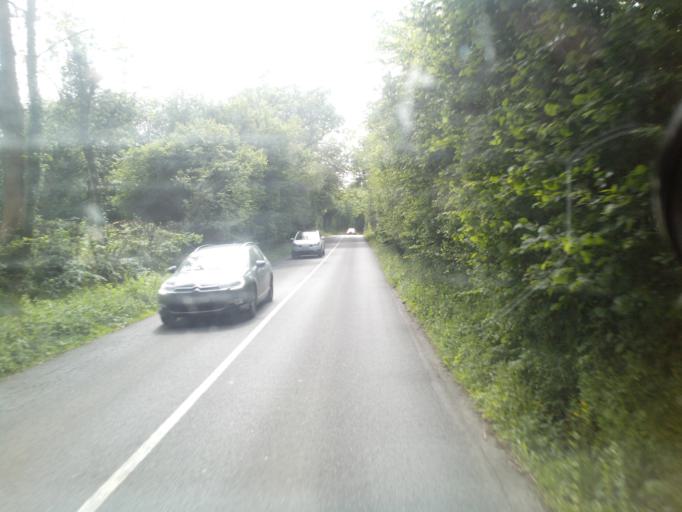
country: FR
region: Lower Normandy
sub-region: Departement du Calvados
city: Dozule
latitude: 49.2542
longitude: -0.0676
